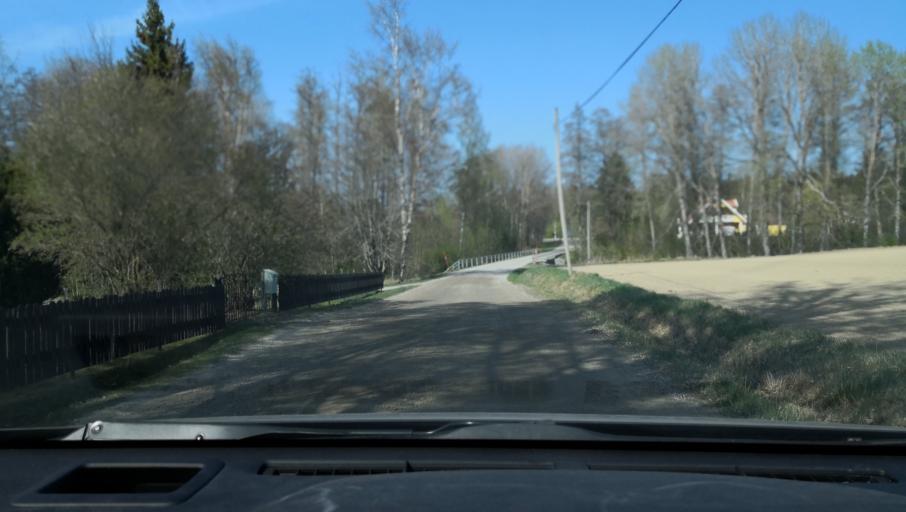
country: SE
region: Uppsala
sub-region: Heby Kommun
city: Heby
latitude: 60.0341
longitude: 16.7828
